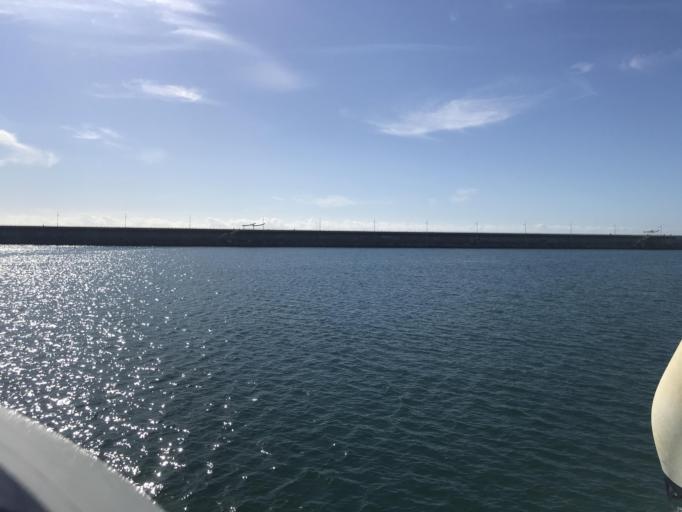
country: ES
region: Valencia
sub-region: Provincia de Alicante
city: Torrevieja
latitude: 37.9684
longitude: -0.6865
